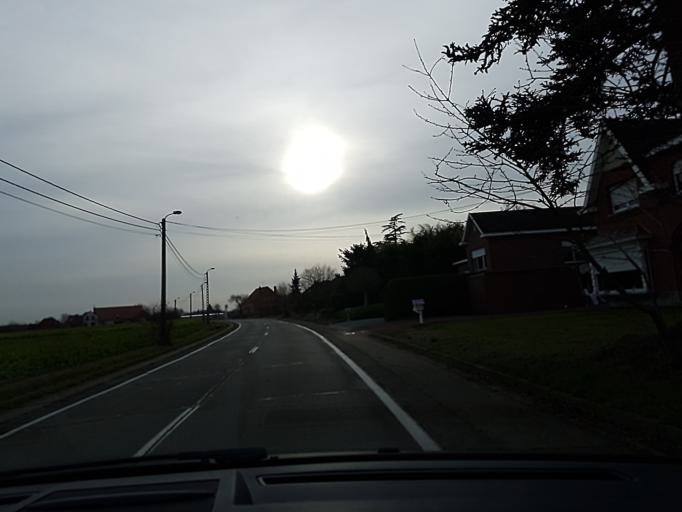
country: BE
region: Flanders
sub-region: Provincie Antwerpen
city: Putte
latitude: 51.0822
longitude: 4.6163
